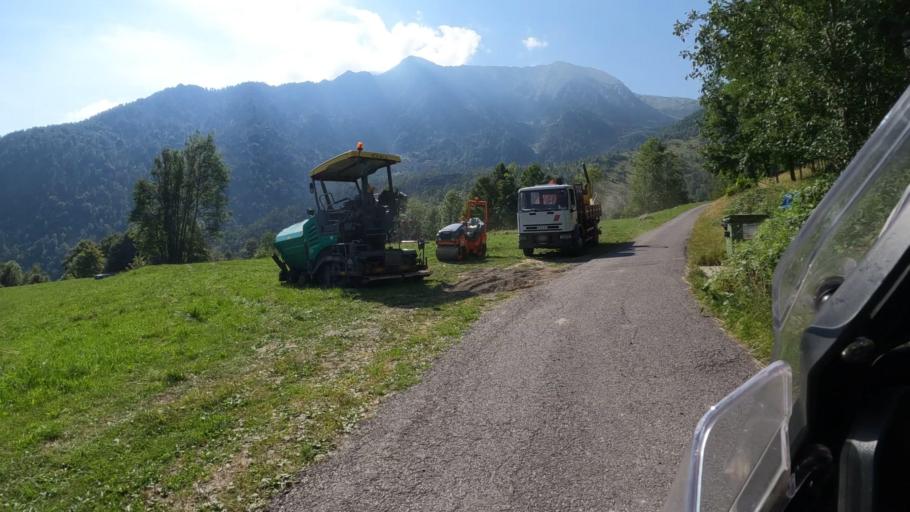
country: IT
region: Piedmont
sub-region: Provincia di Torino
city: Lemie
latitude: 45.2114
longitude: 7.3098
